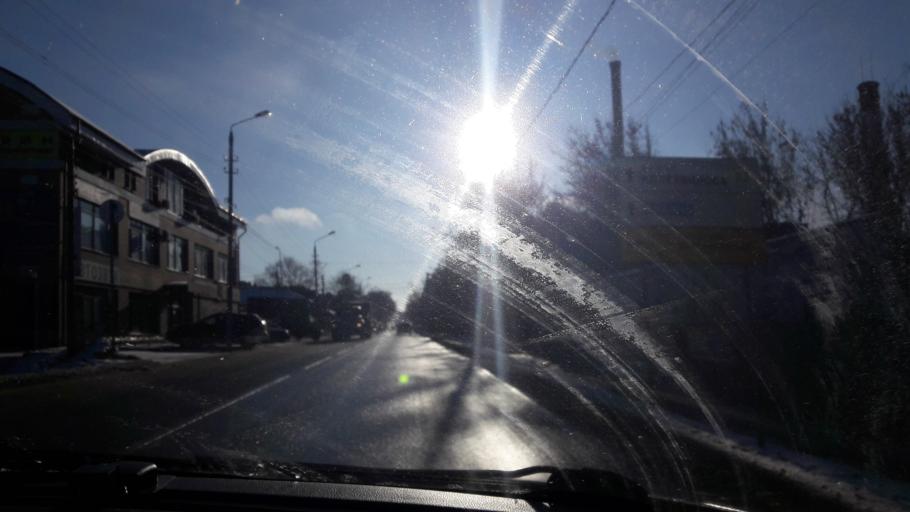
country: RU
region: Tula
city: Tula
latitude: 54.1879
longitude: 37.6258
